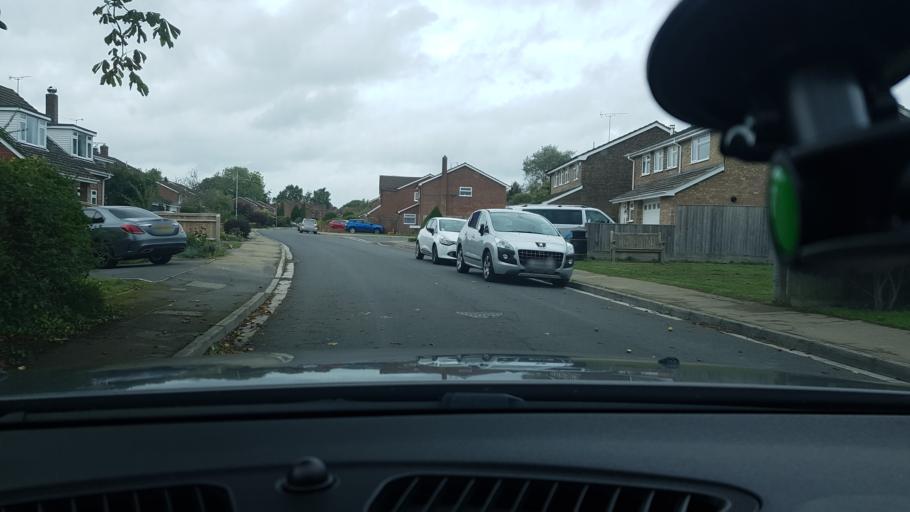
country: GB
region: England
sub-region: Wiltshire
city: Burbage
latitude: 51.3487
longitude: -1.6687
